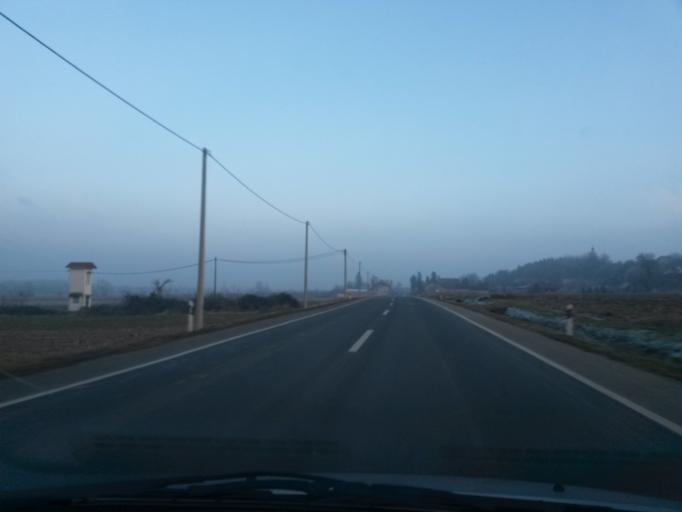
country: HR
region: Varazdinska
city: Ludbreg
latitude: 46.2336
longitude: 16.6529
